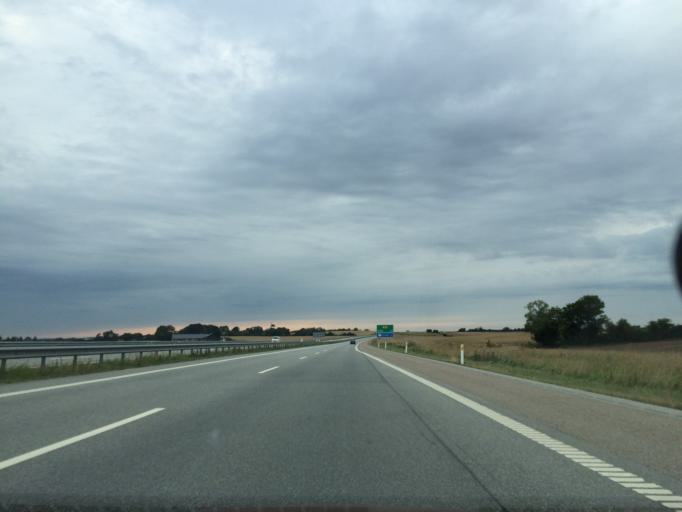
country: DK
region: South Denmark
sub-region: Sonderborg Kommune
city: Broager
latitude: 54.9358
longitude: 9.6866
